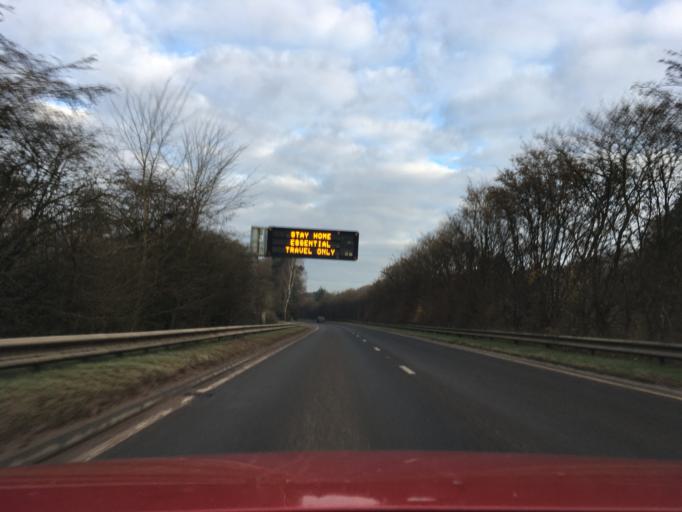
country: GB
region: England
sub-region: Staffordshire
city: Shenstone
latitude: 52.6216
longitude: -1.7982
